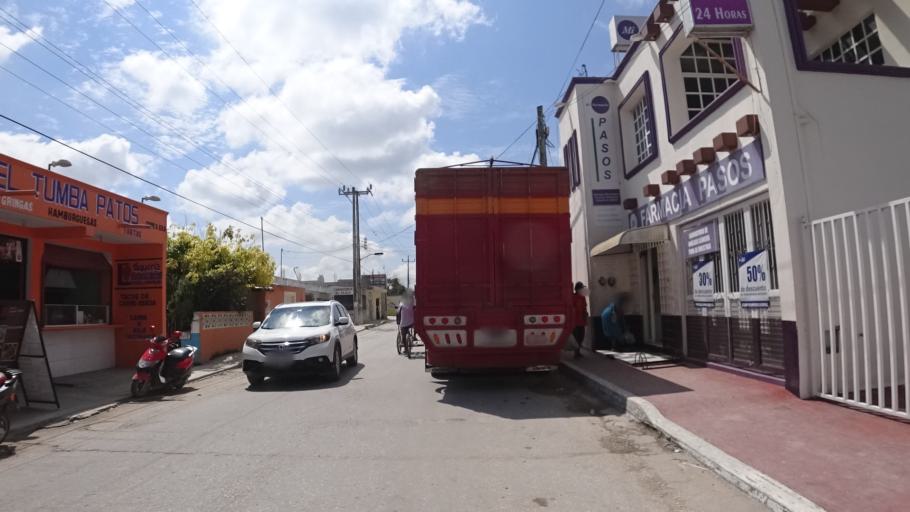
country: MX
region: Campeche
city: Sabancuy
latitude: 18.9719
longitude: -91.1791
